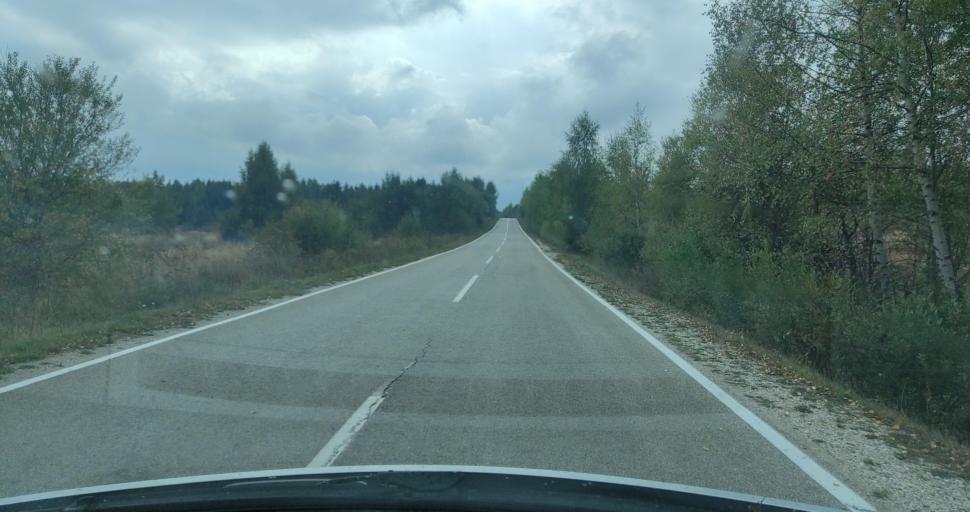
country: RS
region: Central Serbia
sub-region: Jablanicki Okrug
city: Crna Trava
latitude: 42.6939
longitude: 22.3207
